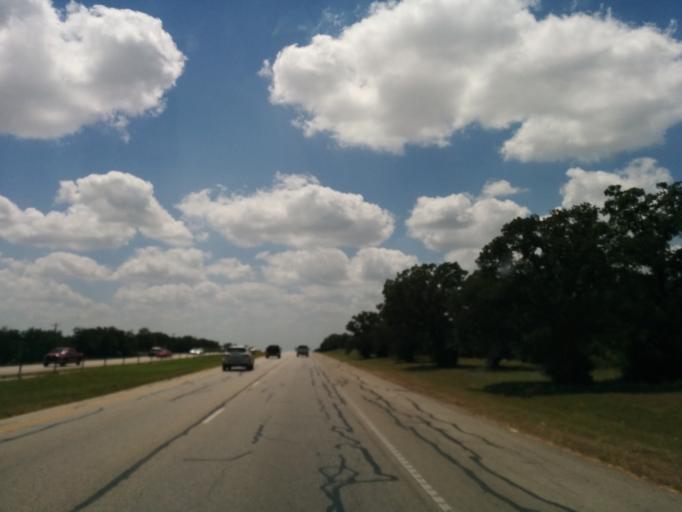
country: US
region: Texas
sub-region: Bastrop County
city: Bastrop
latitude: 30.1110
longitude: -97.3866
